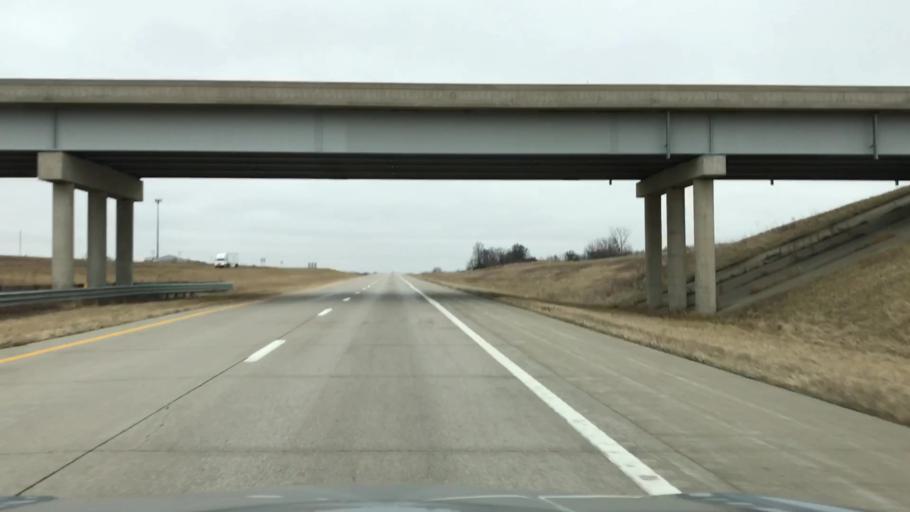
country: US
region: Missouri
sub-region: Linn County
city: Marceline
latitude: 39.7651
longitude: -92.7489
